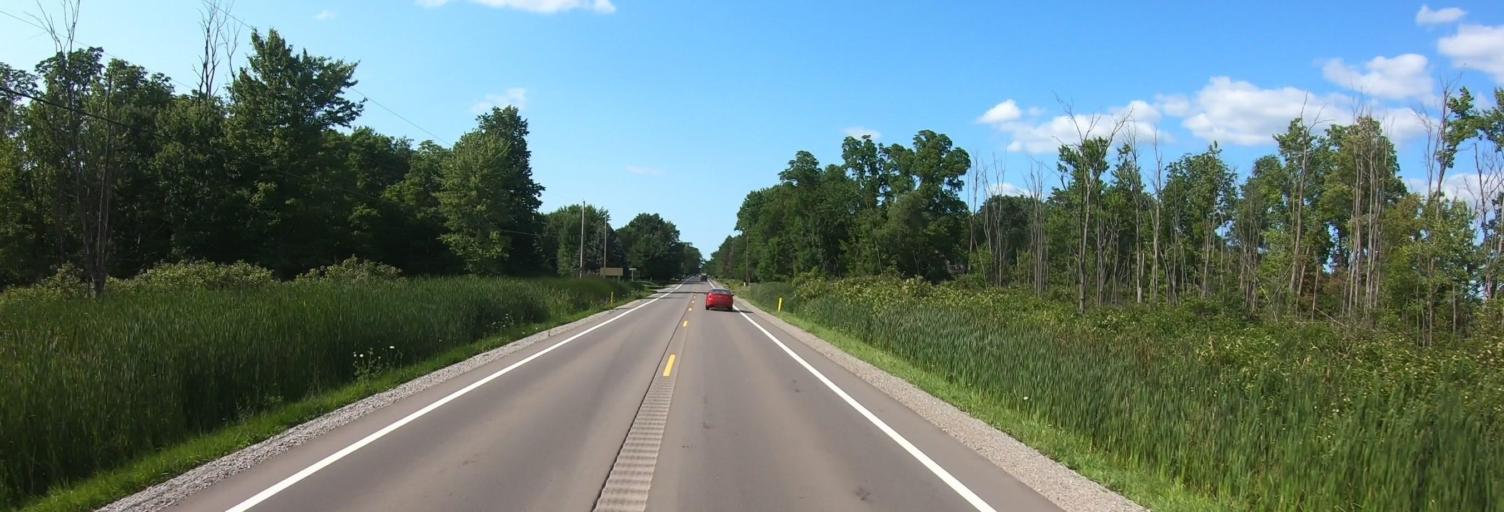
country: US
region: Michigan
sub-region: Oakland County
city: Holly
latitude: 42.8394
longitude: -83.6288
